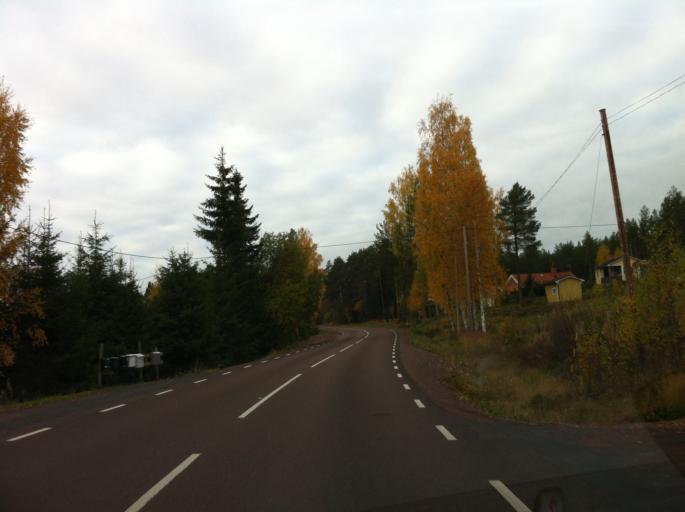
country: SE
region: Dalarna
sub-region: Orsa Kommun
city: Orsa
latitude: 61.1293
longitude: 14.5383
